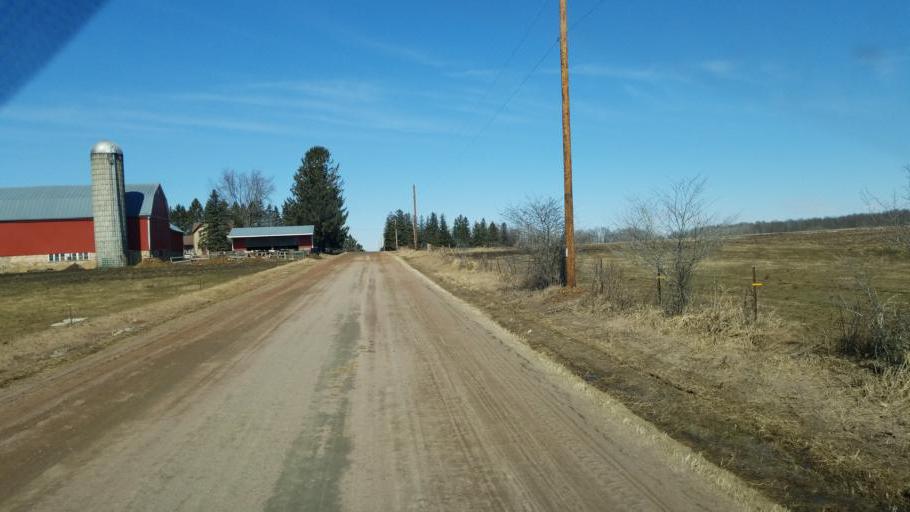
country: US
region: Wisconsin
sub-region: Marathon County
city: Spencer
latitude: 44.6148
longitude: -90.3767
